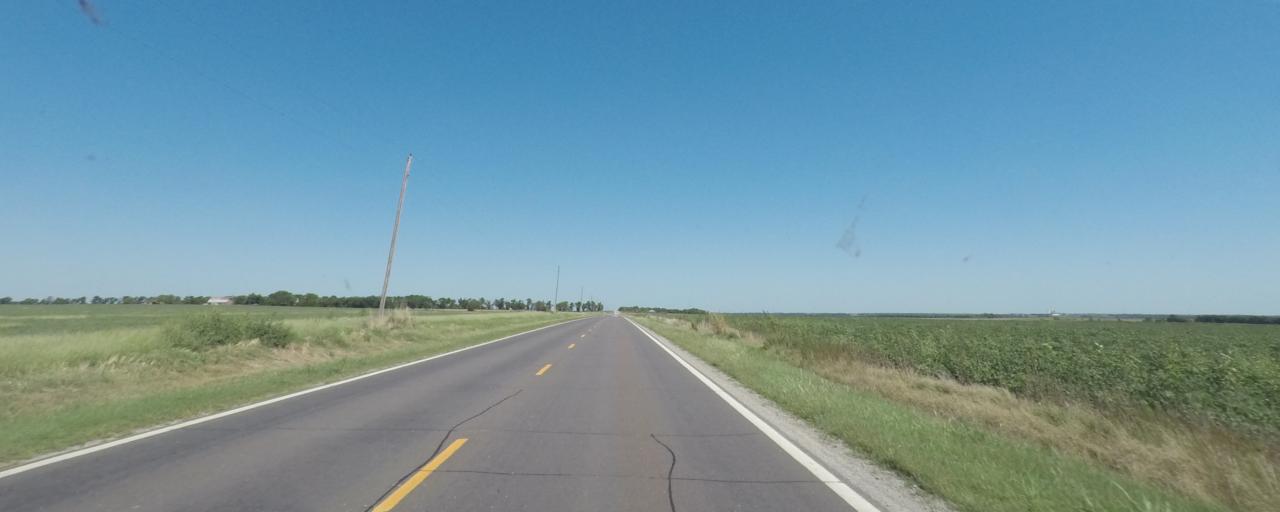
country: US
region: Kansas
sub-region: Sumner County
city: Wellington
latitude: 37.2034
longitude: -97.4023
